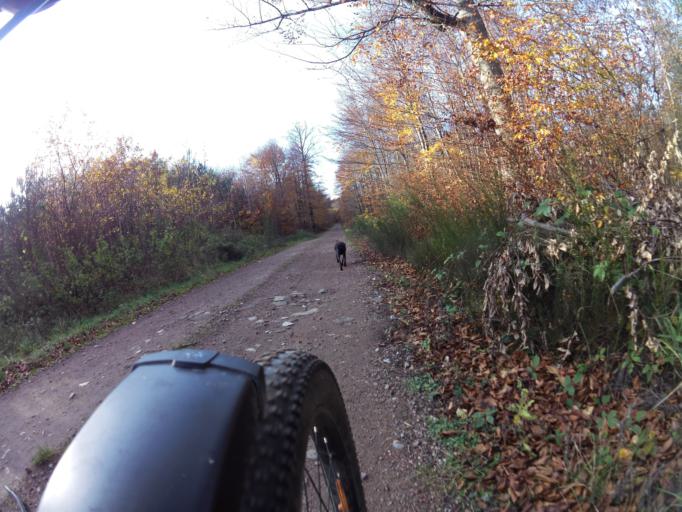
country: PL
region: Pomeranian Voivodeship
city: Strzelno
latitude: 54.7407
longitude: 18.2773
